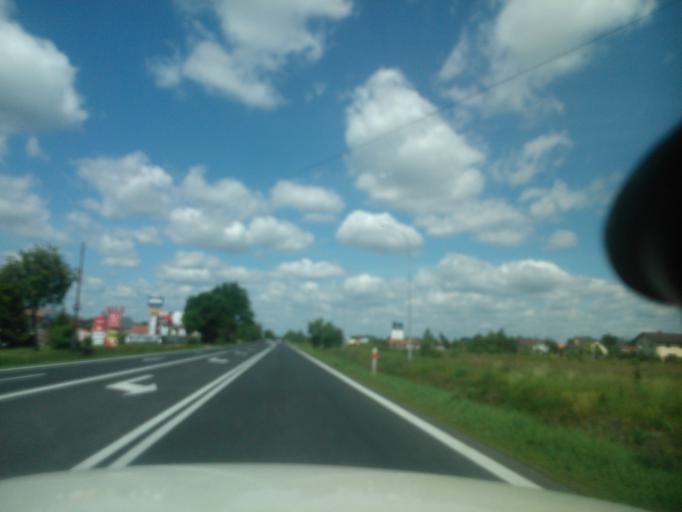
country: PL
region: Kujawsko-Pomorskie
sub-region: Powiat torunski
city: Lubicz Gorny
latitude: 53.0171
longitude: 18.8115
